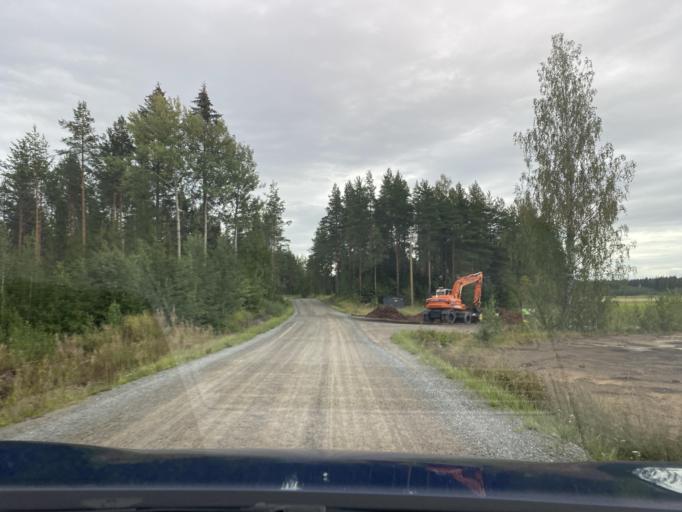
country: FI
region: Pirkanmaa
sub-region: Lounais-Pirkanmaa
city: Punkalaidun
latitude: 61.2502
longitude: 23.0351
